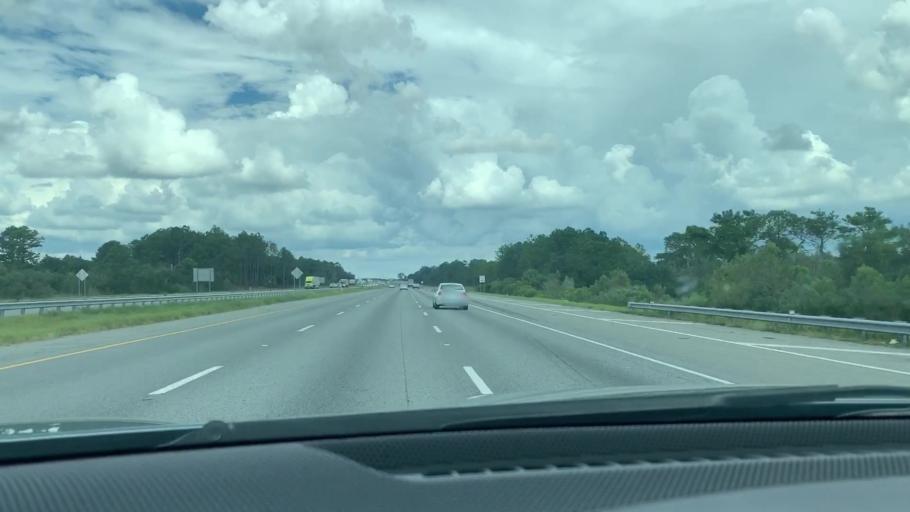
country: US
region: Georgia
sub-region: Glynn County
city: Dock Junction
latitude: 31.1557
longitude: -81.5617
